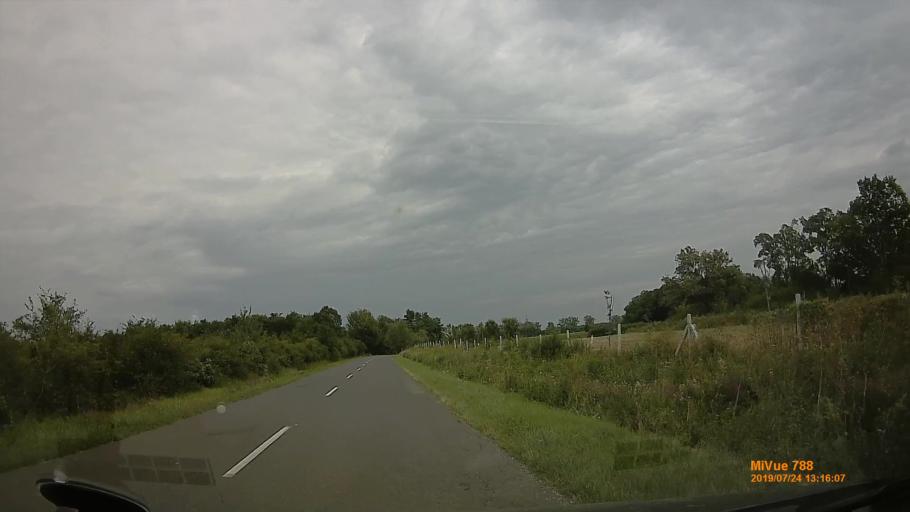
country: HU
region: Szabolcs-Szatmar-Bereg
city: Vasarosnameny
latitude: 48.1940
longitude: 22.3658
